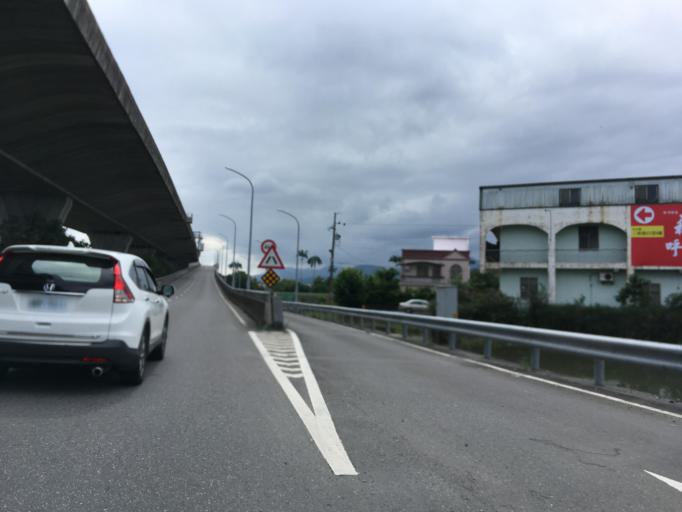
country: TW
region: Taiwan
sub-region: Yilan
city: Yilan
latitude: 24.6645
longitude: 121.7986
